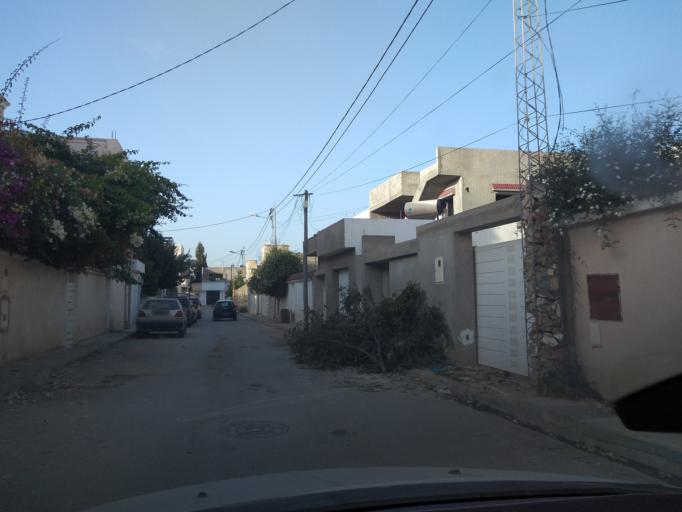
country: TN
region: Manouba
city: Manouba
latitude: 36.7908
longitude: 10.0868
